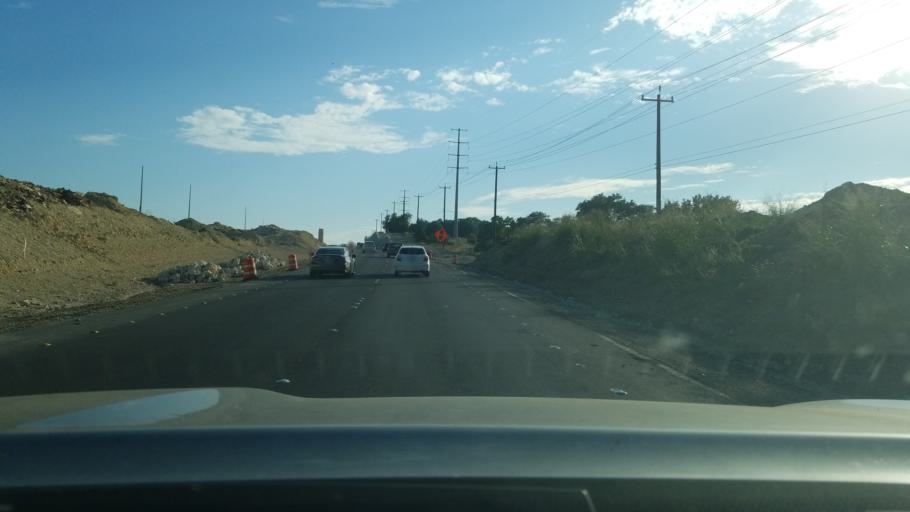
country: US
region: Texas
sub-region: Comal County
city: Bulverde
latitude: 29.7158
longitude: -98.4465
